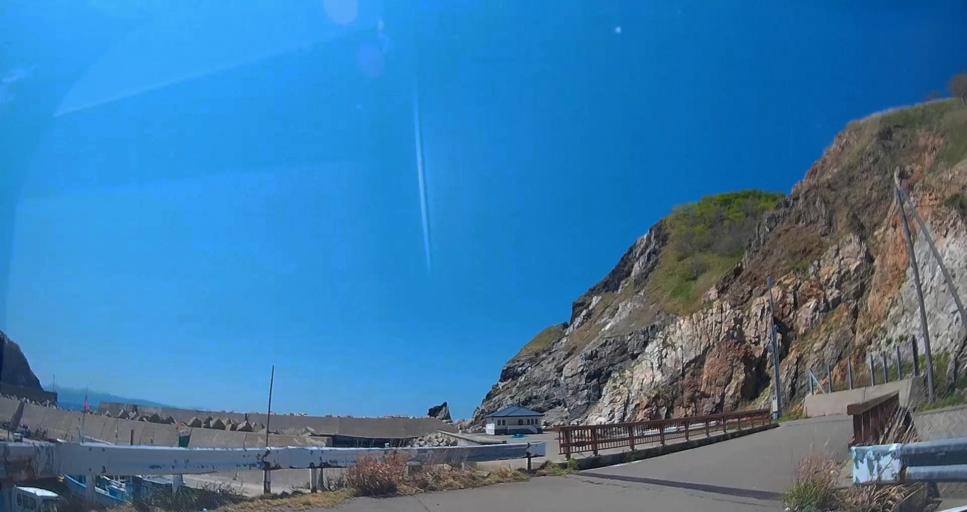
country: JP
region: Aomori
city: Mutsu
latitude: 41.3285
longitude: 140.8068
